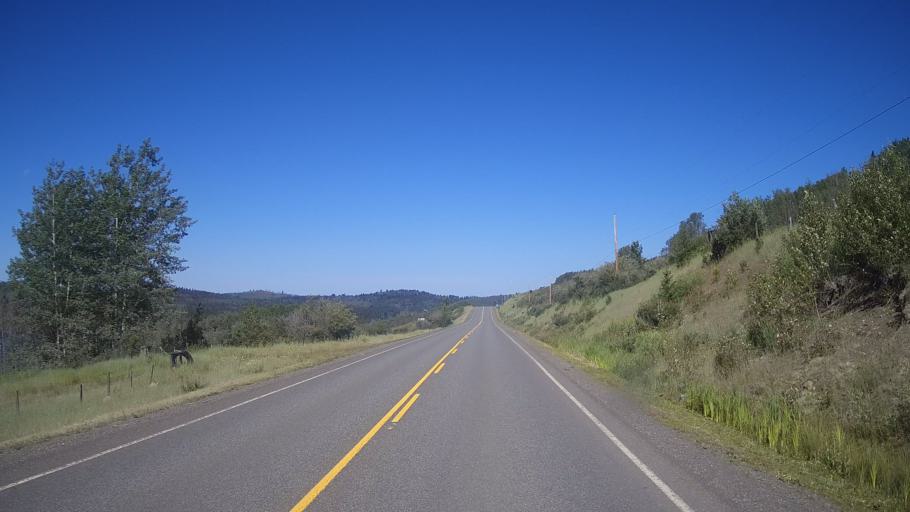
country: CA
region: British Columbia
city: Kamloops
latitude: 51.4967
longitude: -120.5825
